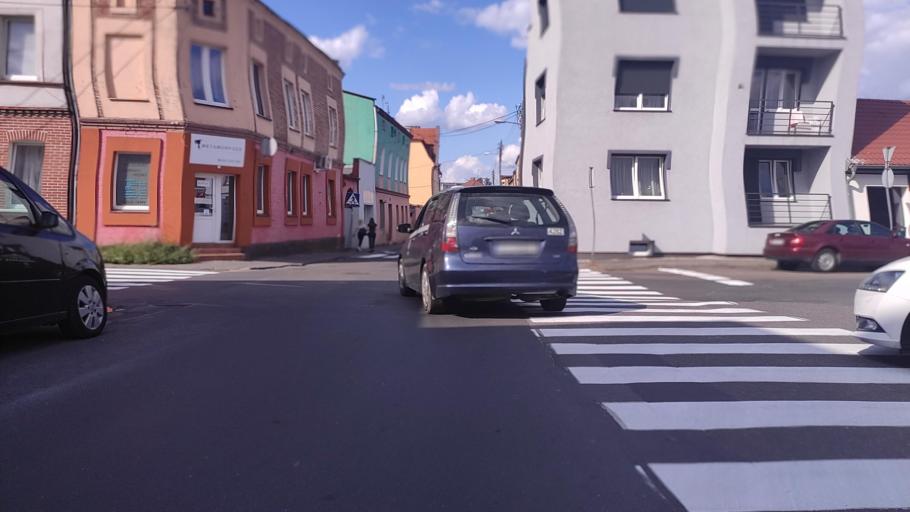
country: PL
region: Greater Poland Voivodeship
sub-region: Powiat poznanski
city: Swarzedz
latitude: 52.4115
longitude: 17.0771
